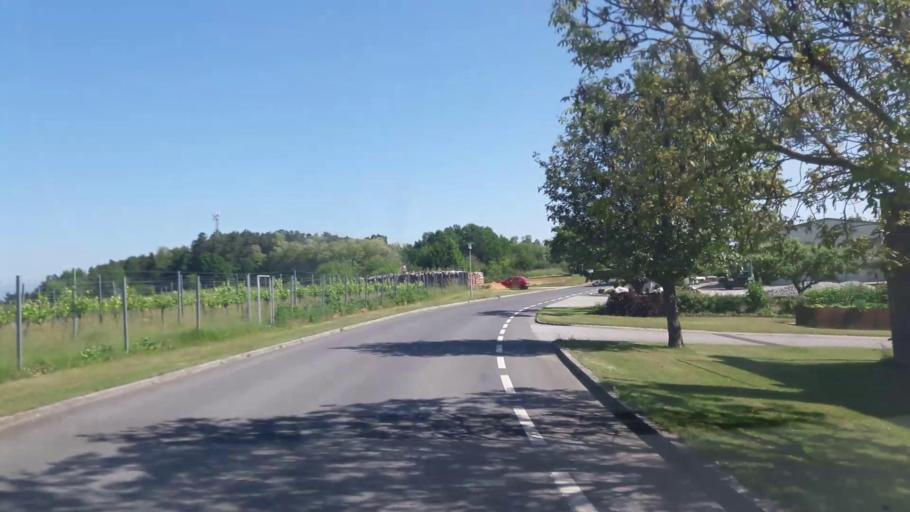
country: AT
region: Styria
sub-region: Politischer Bezirk Hartberg-Fuerstenfeld
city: Neudau
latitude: 47.1635
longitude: 16.1224
